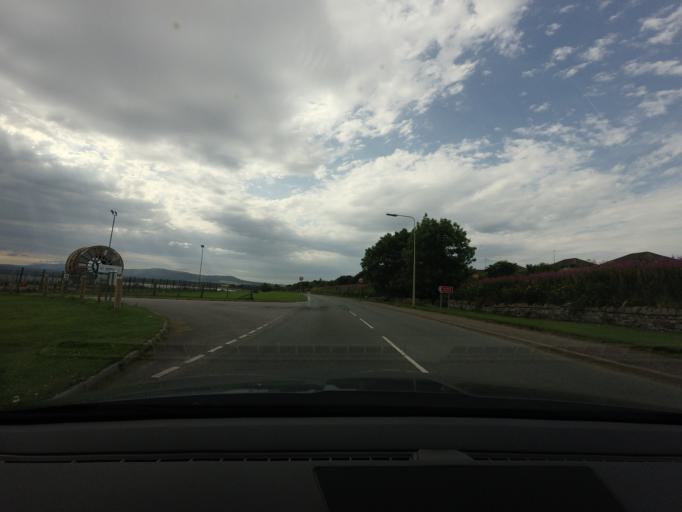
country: GB
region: Scotland
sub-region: Highland
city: Invergordon
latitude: 57.6887
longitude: -4.1784
